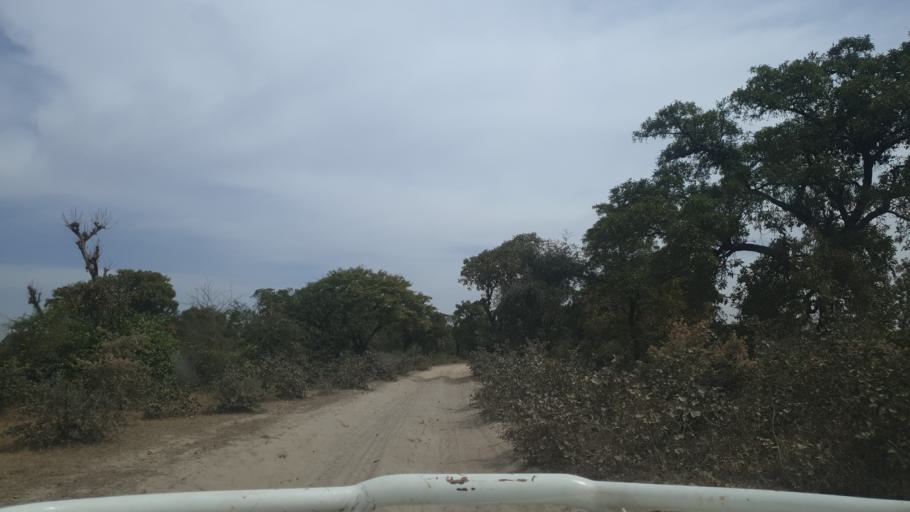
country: ML
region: Sikasso
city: Yorosso
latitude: 12.2365
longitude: -4.7414
